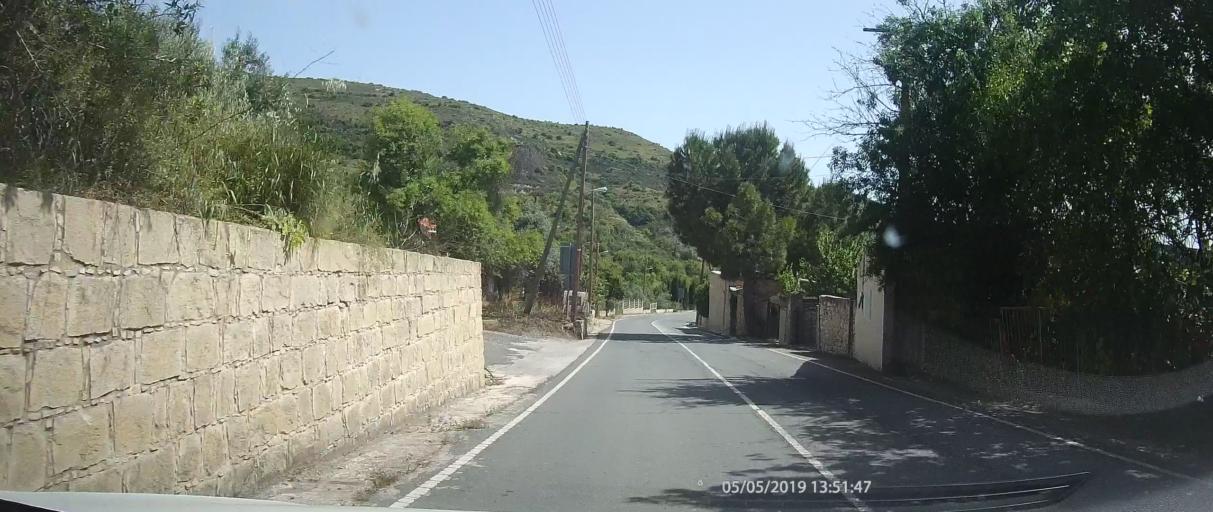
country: CY
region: Limassol
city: Pachna
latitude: 34.8351
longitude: 32.7363
